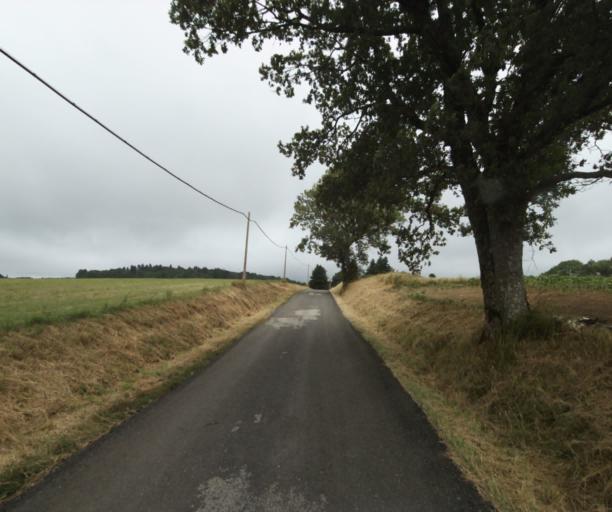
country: FR
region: Midi-Pyrenees
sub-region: Departement du Tarn
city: Soreze
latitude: 43.4078
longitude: 2.0732
